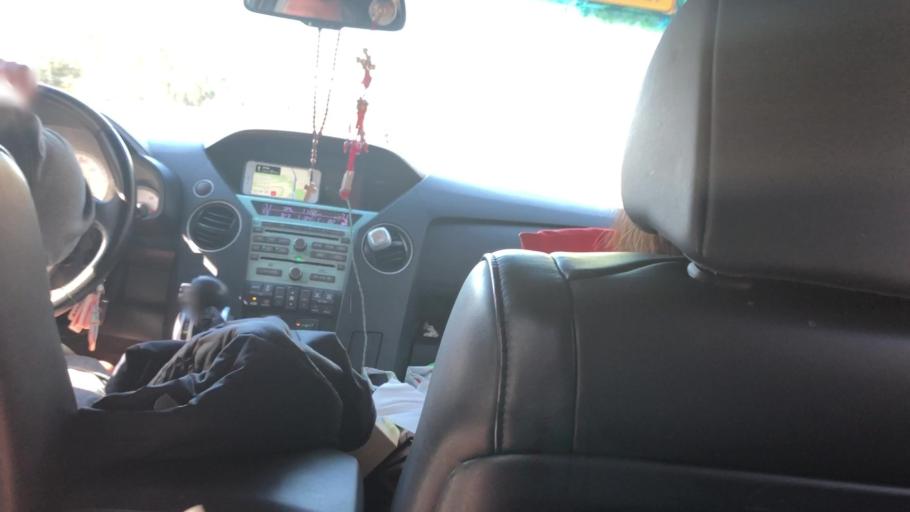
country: US
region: Louisiana
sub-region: Saint John the Baptist Parish
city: Montegut
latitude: 30.1024
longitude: -90.4875
